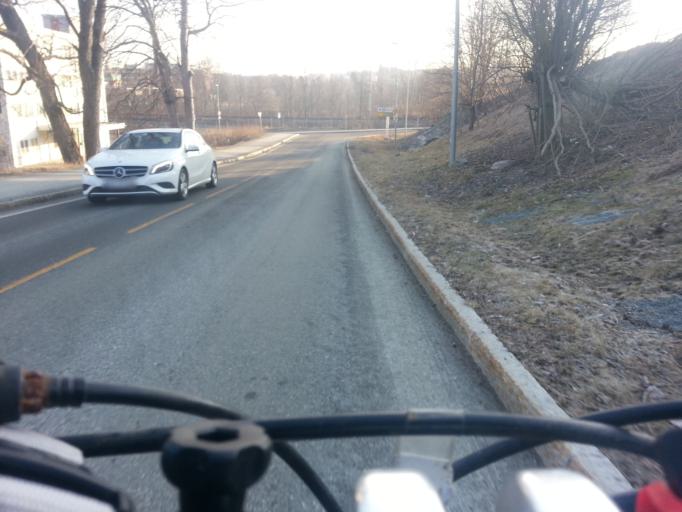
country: NO
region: Sor-Trondelag
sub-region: Trondheim
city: Trondheim
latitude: 63.4164
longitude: 10.3811
